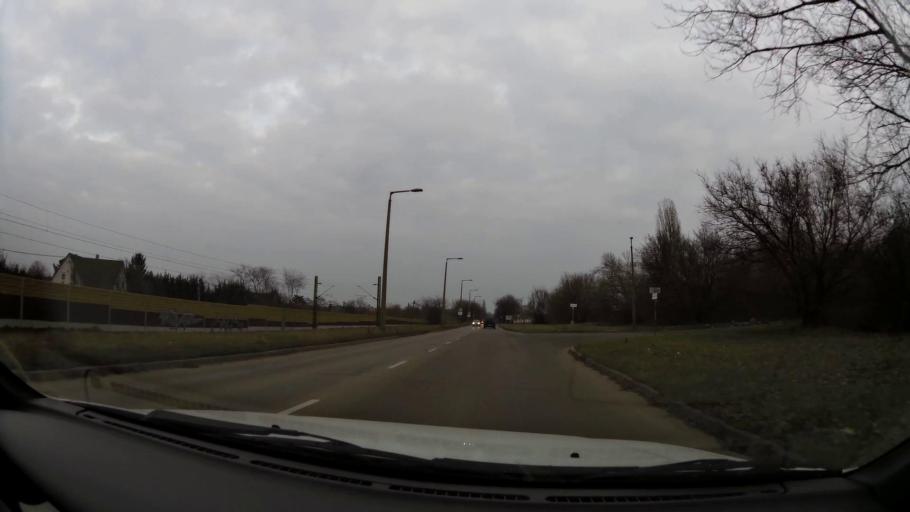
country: HU
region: Budapest
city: Budapest X. keruelet
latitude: 47.4836
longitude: 19.1998
